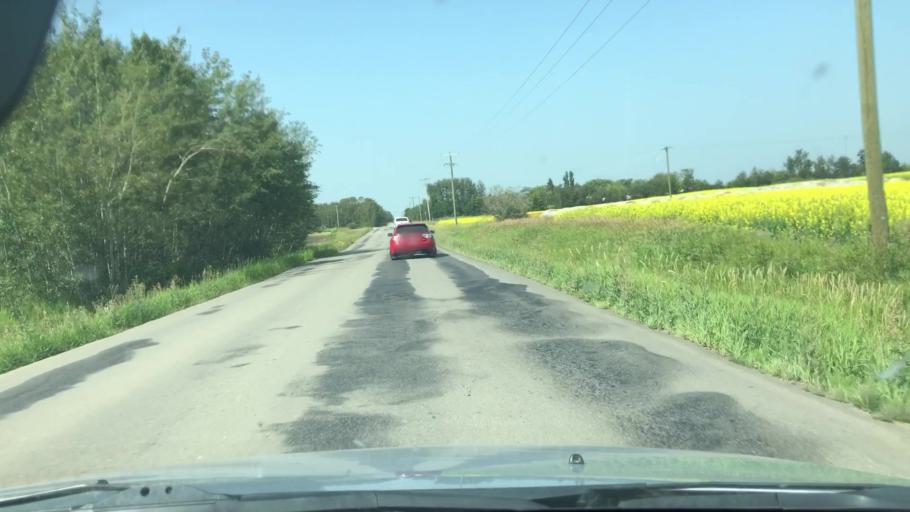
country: CA
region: Alberta
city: Devon
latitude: 53.5122
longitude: -113.7205
